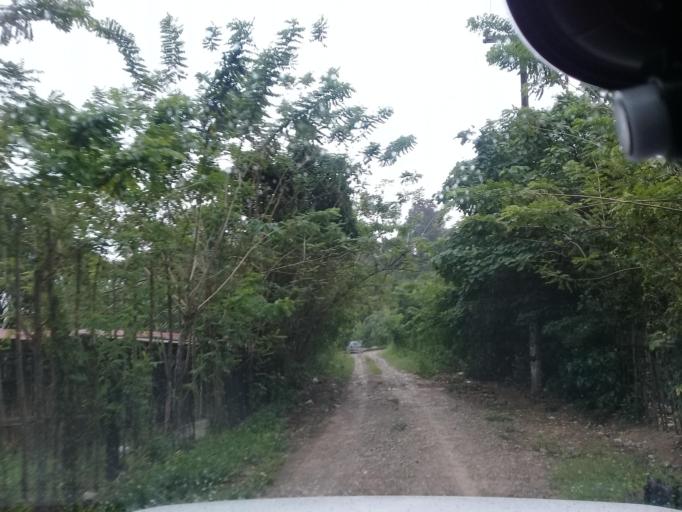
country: MX
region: Veracruz
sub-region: Chalma
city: San Pedro Coyutla
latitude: 21.2425
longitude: -98.4203
